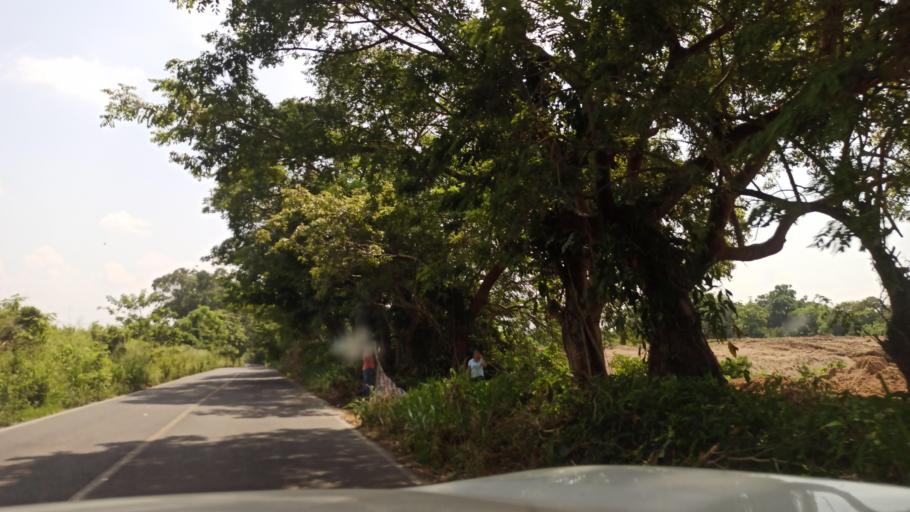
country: MX
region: Veracruz
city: Martinez de la Torre
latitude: 20.0867
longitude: -97.0788
